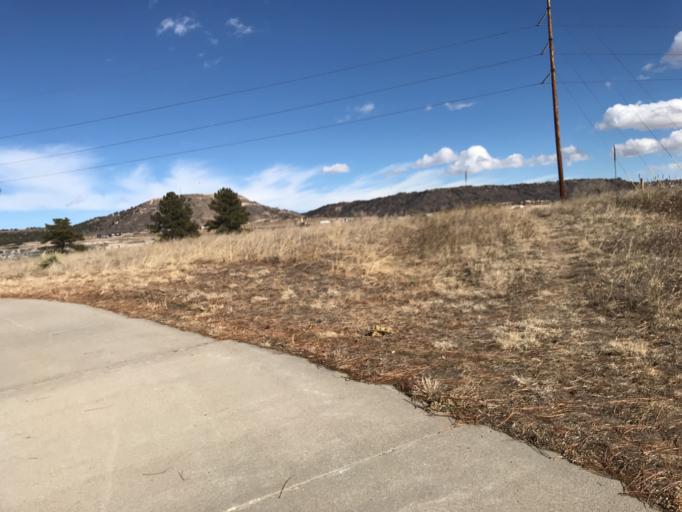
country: US
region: Colorado
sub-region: Douglas County
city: Castle Pines
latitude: 39.4132
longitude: -104.8885
